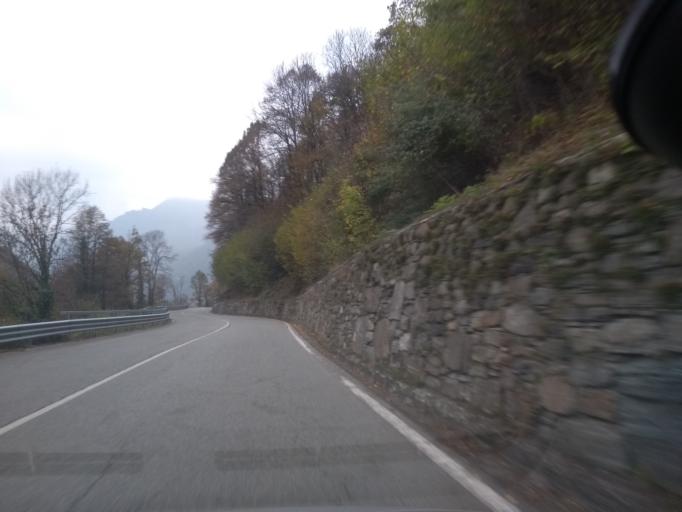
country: IT
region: Piedmont
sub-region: Provincia di Torino
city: Ceres
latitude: 45.3179
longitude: 7.3963
